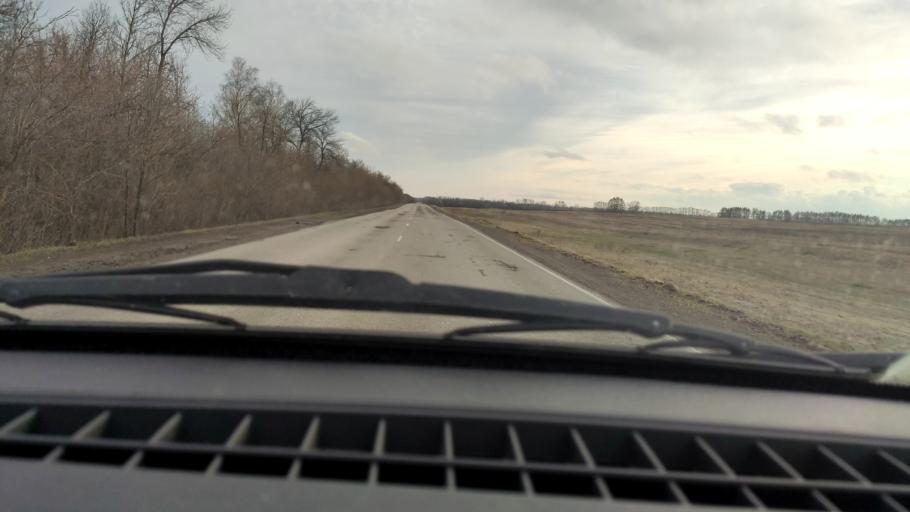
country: RU
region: Bashkortostan
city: Chishmy
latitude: 54.4737
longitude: 55.2642
